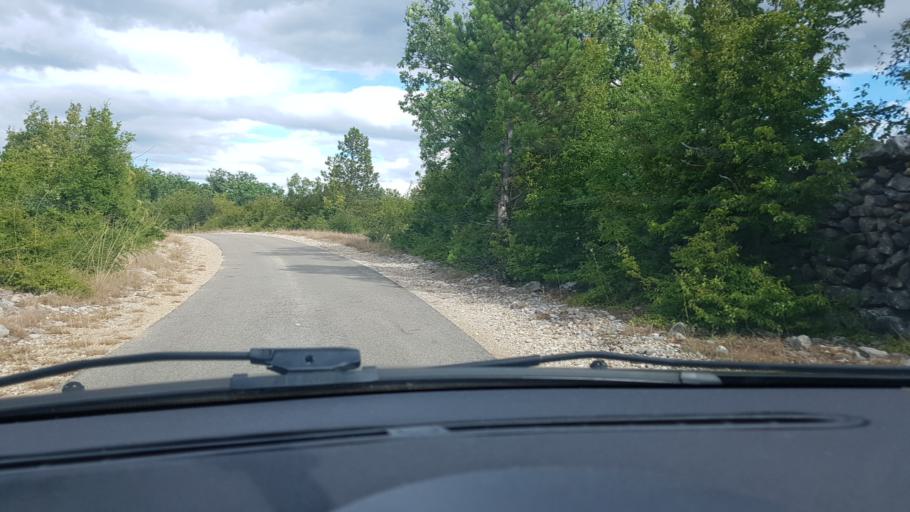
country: HR
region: Sibensko-Kniniska
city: Kistanje
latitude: 44.1109
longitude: 15.9202
